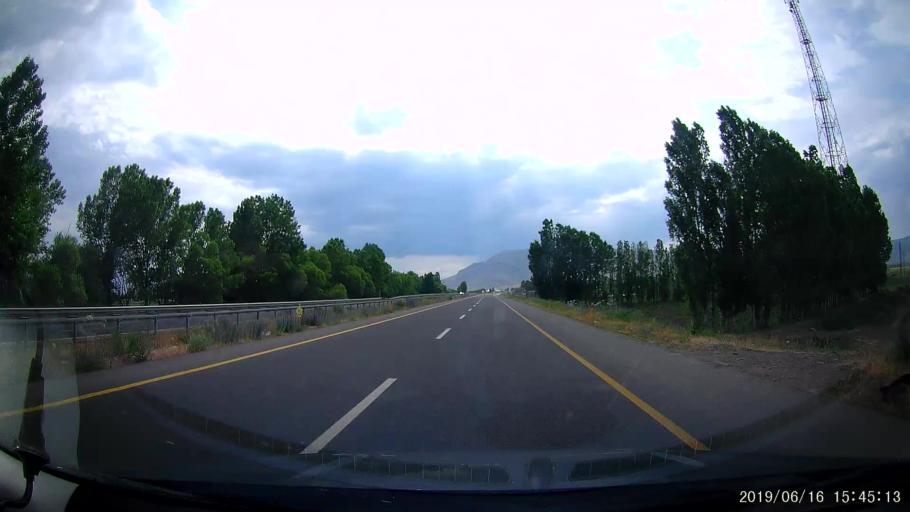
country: TR
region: Erzurum
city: Koprukoy
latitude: 39.9880
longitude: 41.7714
